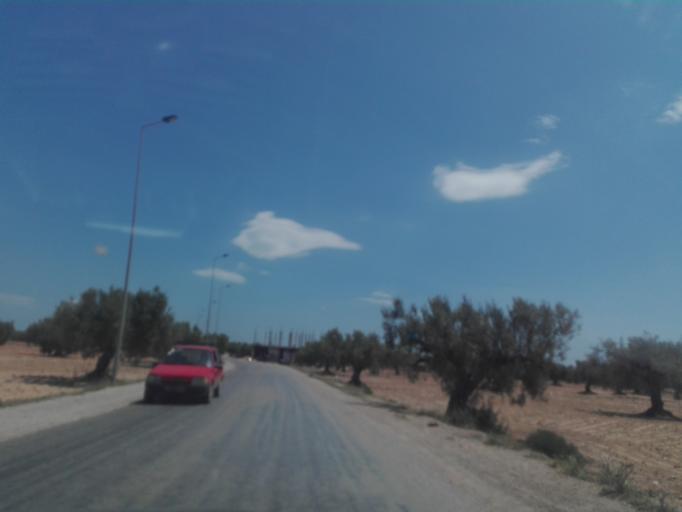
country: TN
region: Safaqis
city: Sfax
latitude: 34.6248
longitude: 10.6018
